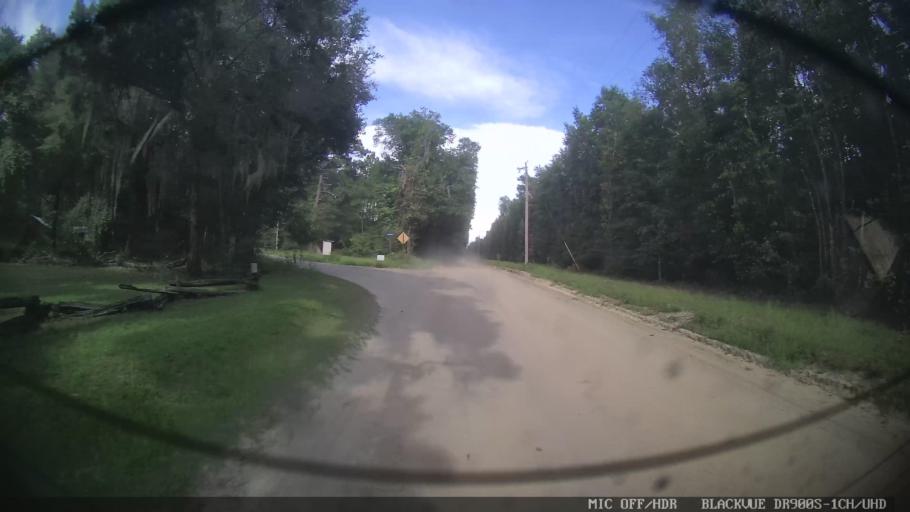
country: US
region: Georgia
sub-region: Lowndes County
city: Valdosta
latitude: 30.6206
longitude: -83.2523
